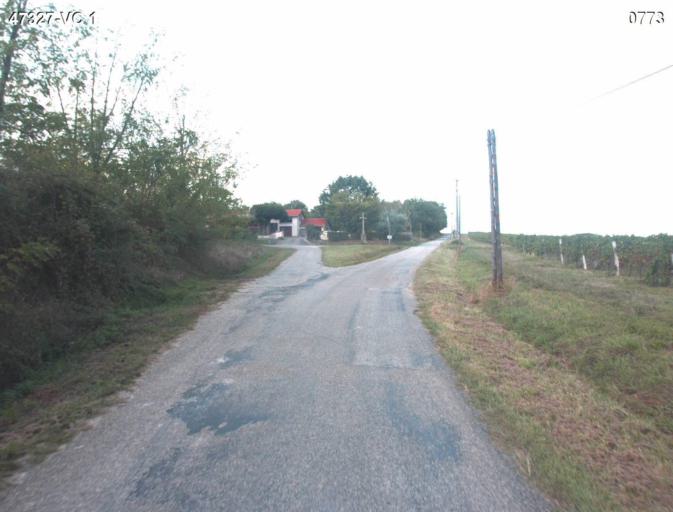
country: FR
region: Aquitaine
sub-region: Departement du Lot-et-Garonne
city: Barbaste
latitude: 44.1918
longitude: 0.2555
